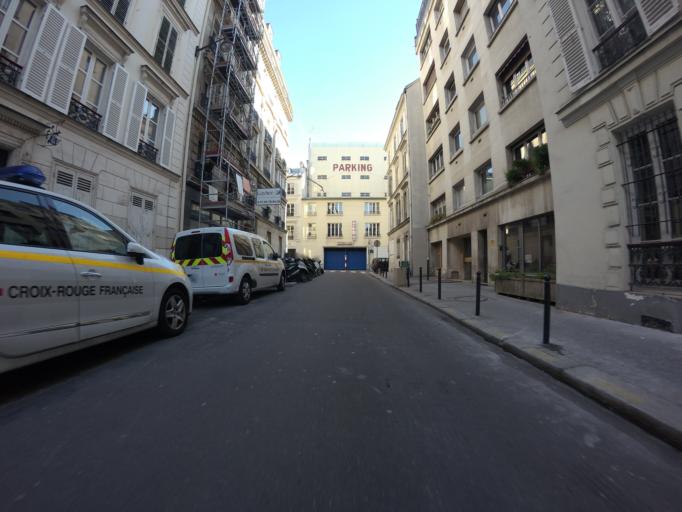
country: FR
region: Ile-de-France
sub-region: Departement des Hauts-de-Seine
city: Clichy
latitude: 48.8835
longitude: 2.3154
